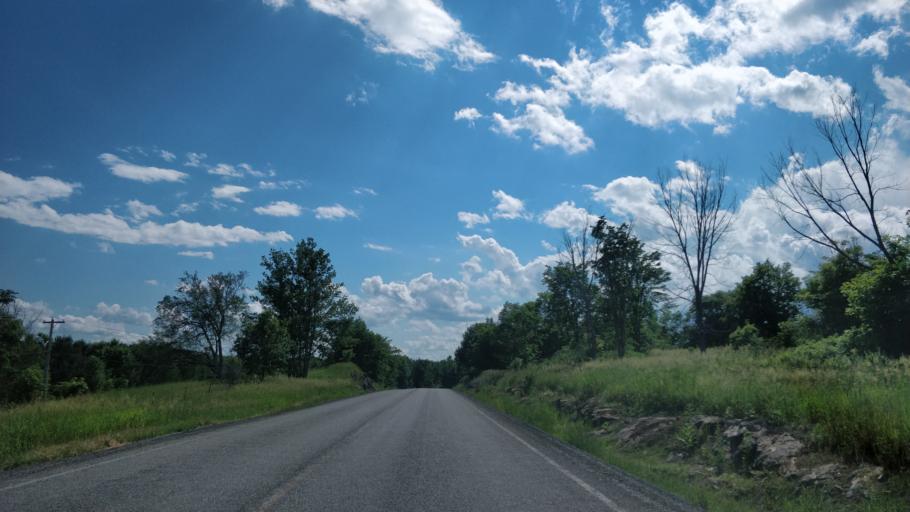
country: CA
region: Ontario
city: Perth
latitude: 44.7696
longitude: -76.4551
